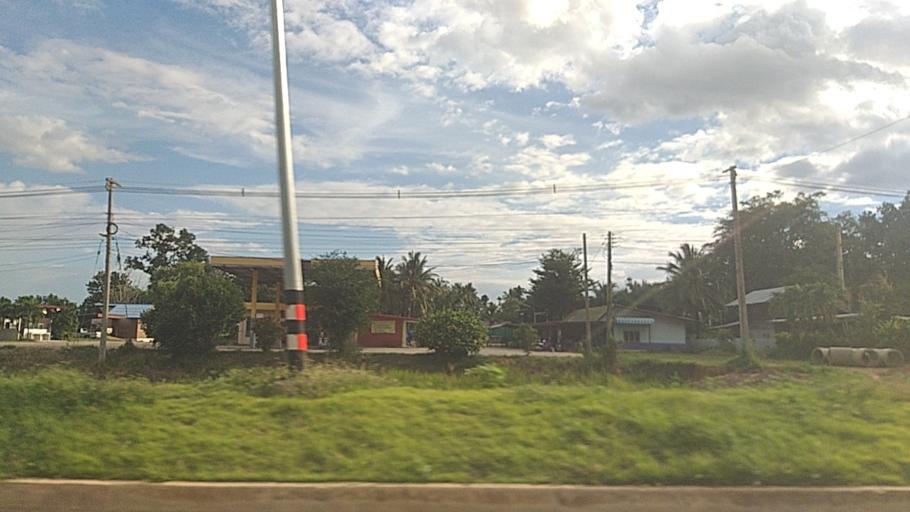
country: TH
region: Surin
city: Kap Choeng
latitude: 14.5255
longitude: 103.5365
